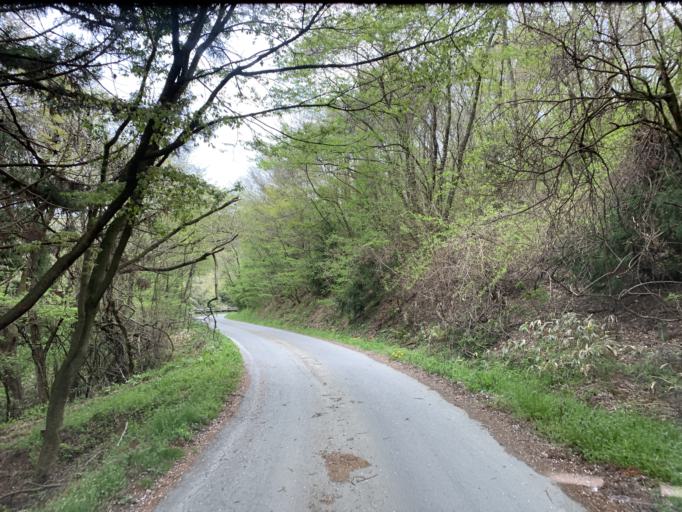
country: JP
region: Iwate
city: Ichinoseki
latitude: 38.7871
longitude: 141.4207
